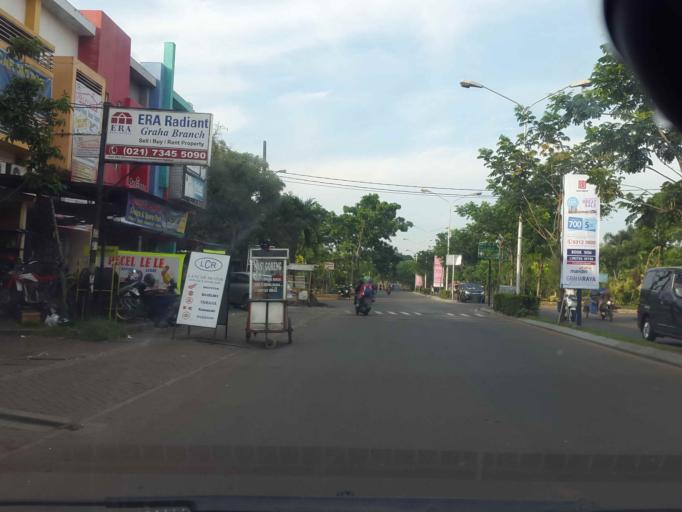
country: ID
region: West Java
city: Ciputat
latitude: -6.2608
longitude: 106.6863
